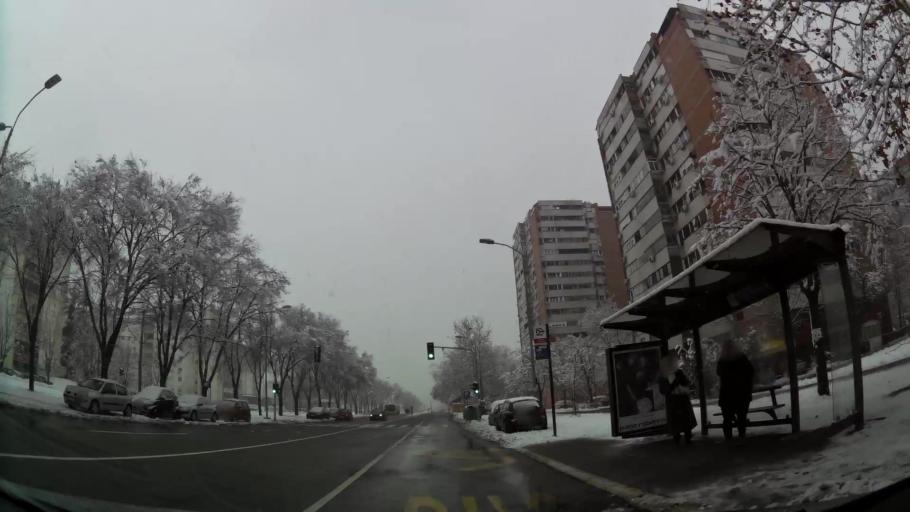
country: RS
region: Central Serbia
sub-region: Belgrade
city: Cukarica
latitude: 44.7958
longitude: 20.3730
